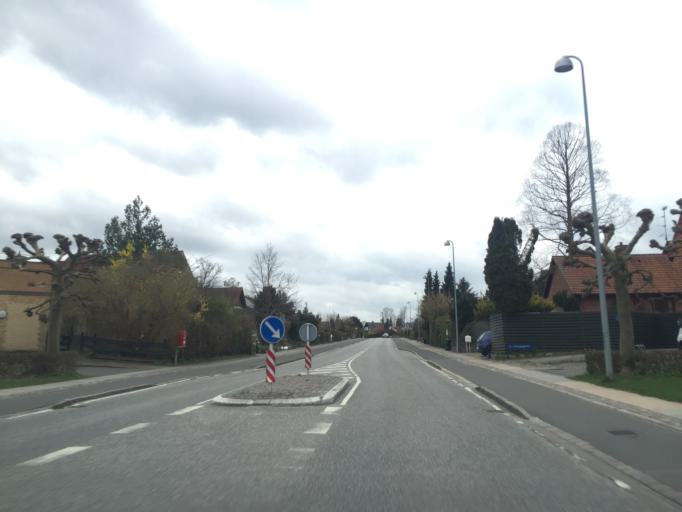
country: DK
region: Capital Region
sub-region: Rudersdal Kommune
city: Holte
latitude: 55.7944
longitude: 12.4647
